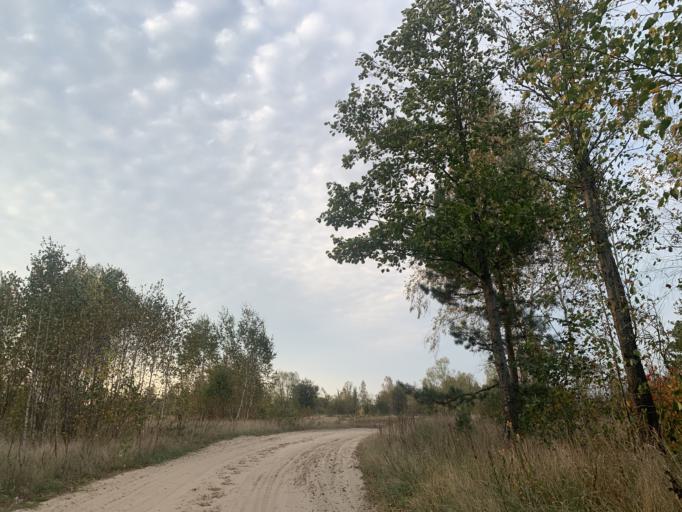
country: BY
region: Brest
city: Mikashevichy
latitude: 52.3306
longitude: 27.4976
